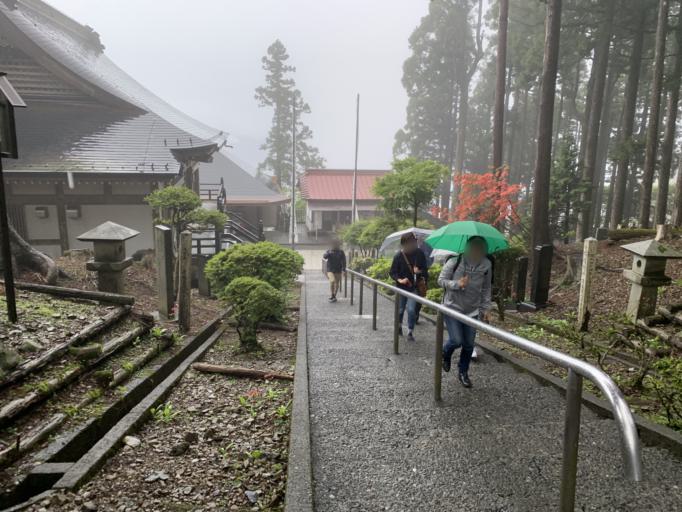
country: JP
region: Yamanashi
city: Ryuo
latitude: 35.3967
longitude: 138.4174
